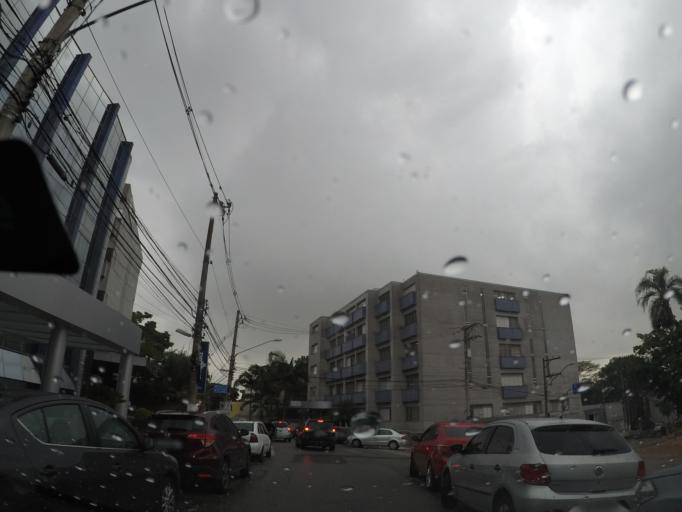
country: BR
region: Sao Paulo
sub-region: Diadema
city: Diadema
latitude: -23.6438
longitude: -46.6426
